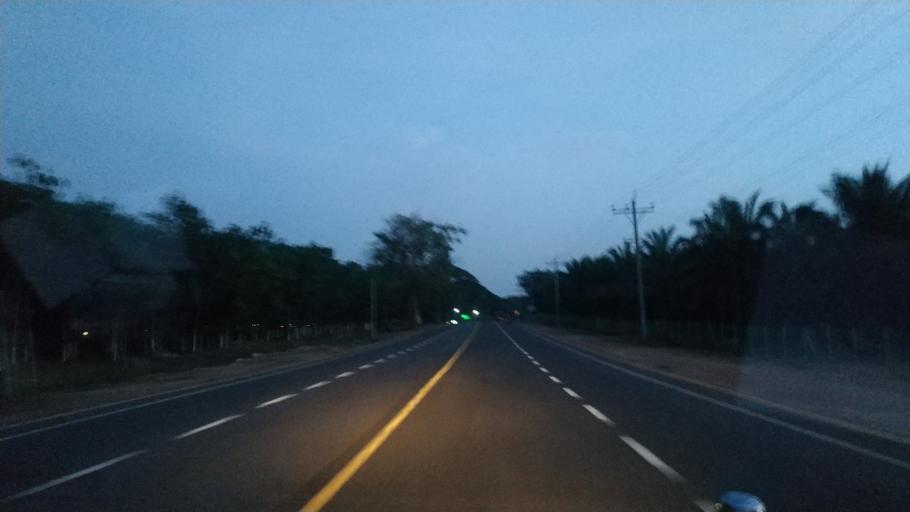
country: MM
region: Mon
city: Kyaikto
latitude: 17.3698
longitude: 97.0494
